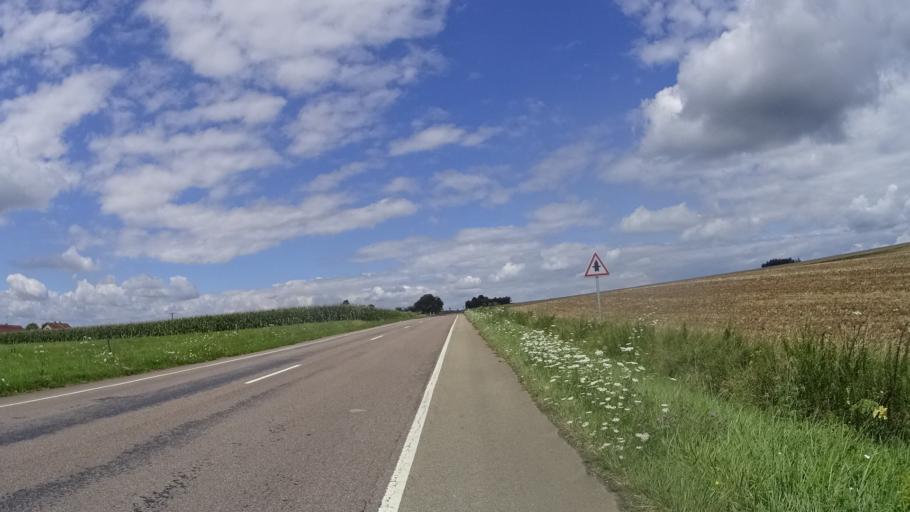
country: FR
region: Champagne-Ardenne
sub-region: Departement de la Haute-Marne
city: Montier-en-Der
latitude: 48.4900
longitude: 4.7578
